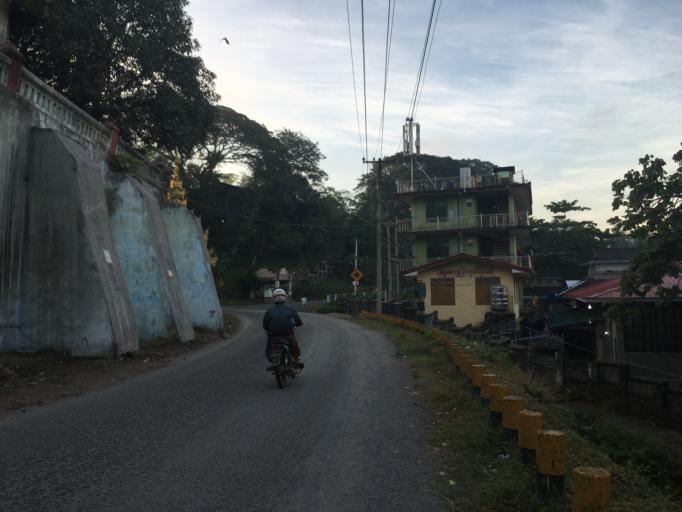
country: MM
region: Mon
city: Mawlamyine
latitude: 16.4884
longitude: 97.6280
